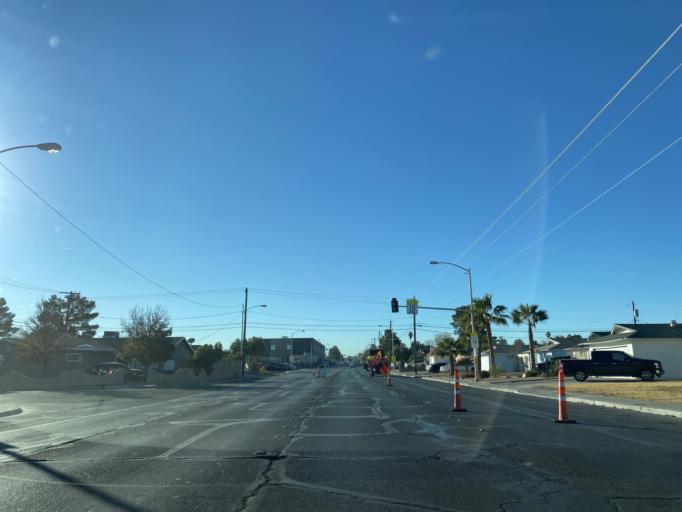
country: US
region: Nevada
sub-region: Clark County
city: Winchester
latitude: 36.1257
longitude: -115.0919
